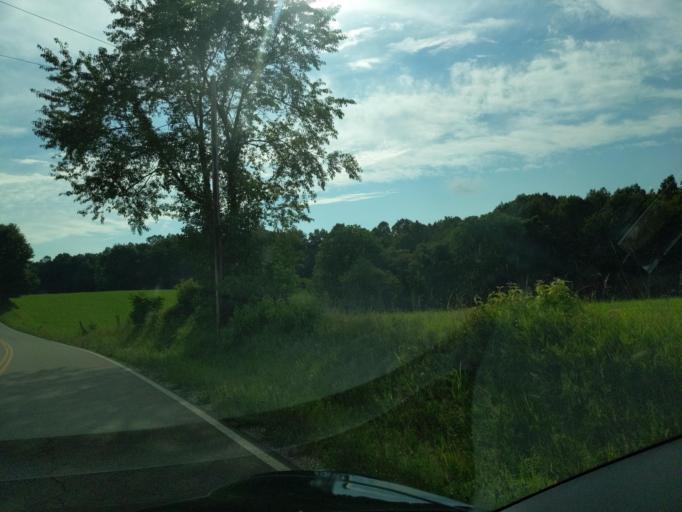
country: US
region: Ohio
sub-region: Fairfield County
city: Lancaster
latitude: 39.5759
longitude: -82.5736
